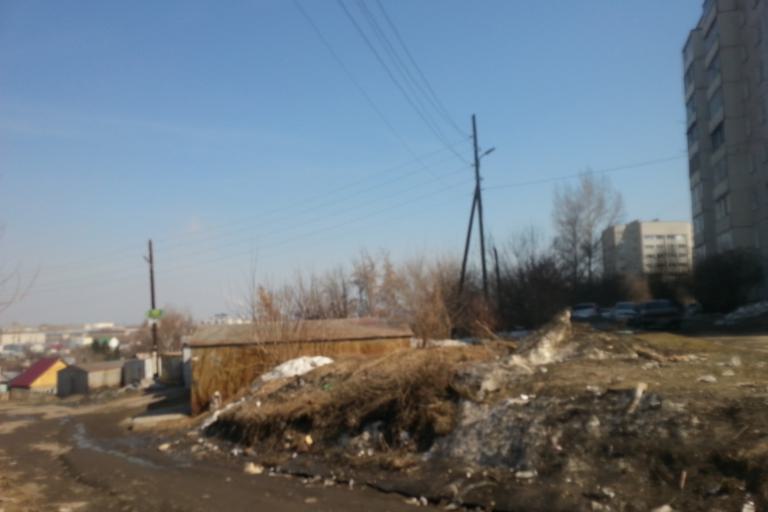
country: RU
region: Altai Krai
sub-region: Gorod Barnaulskiy
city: Barnaul
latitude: 53.3745
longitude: 83.6915
